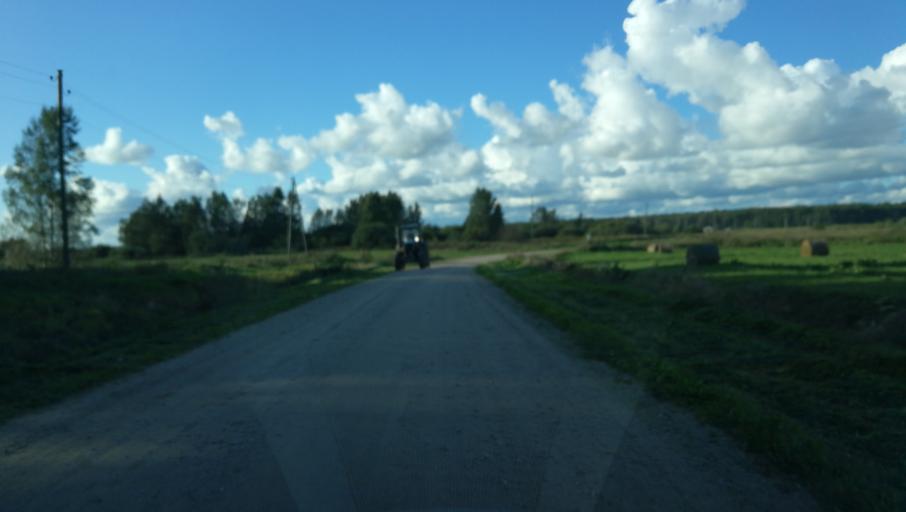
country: LV
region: Riga
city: Jaunciems
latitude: 57.0792
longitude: 24.2279
